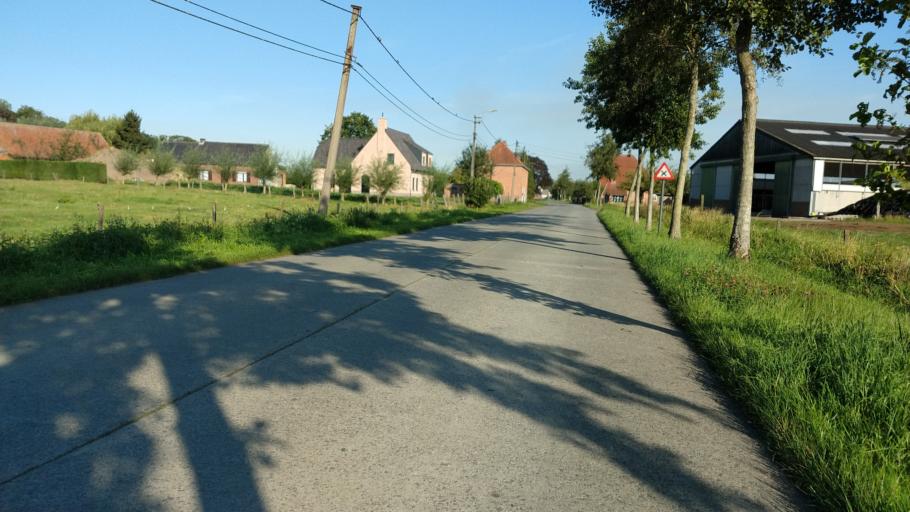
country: BE
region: Flanders
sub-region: Provincie Oost-Vlaanderen
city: Lochristi
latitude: 51.1357
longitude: 3.8308
